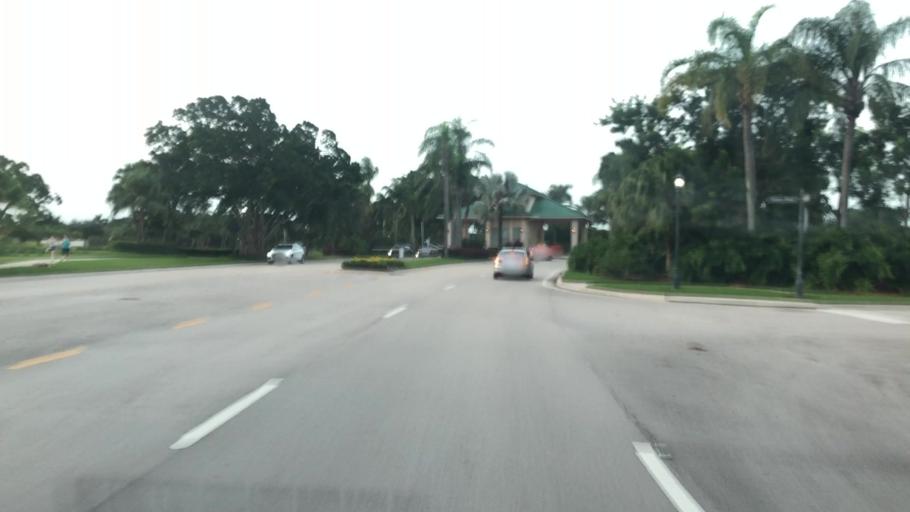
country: US
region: Florida
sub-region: Broward County
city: Weston
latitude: 26.0907
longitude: -80.3918
